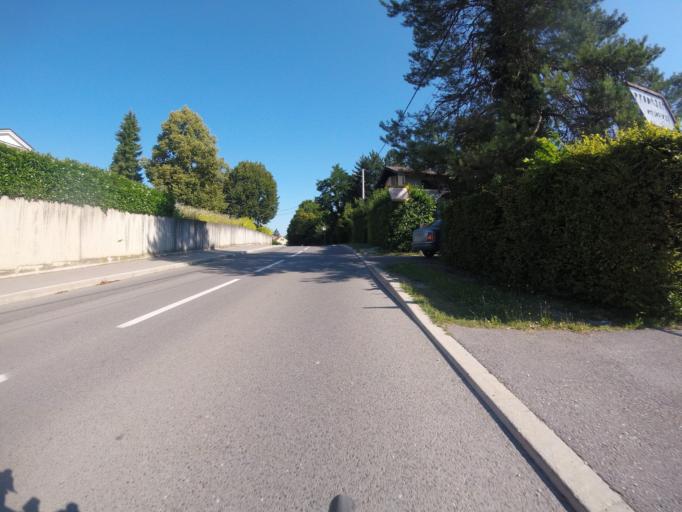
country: HR
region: Zagrebacka
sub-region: Grad Samobor
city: Samobor
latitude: 45.8157
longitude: 15.7047
